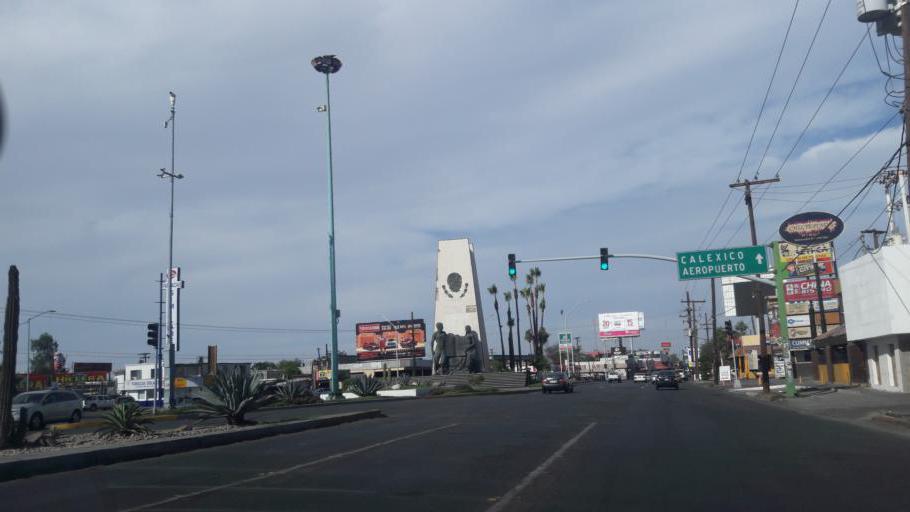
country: MX
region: Baja California
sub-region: Mexicali
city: Mexicali
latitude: 32.6471
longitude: -115.4518
